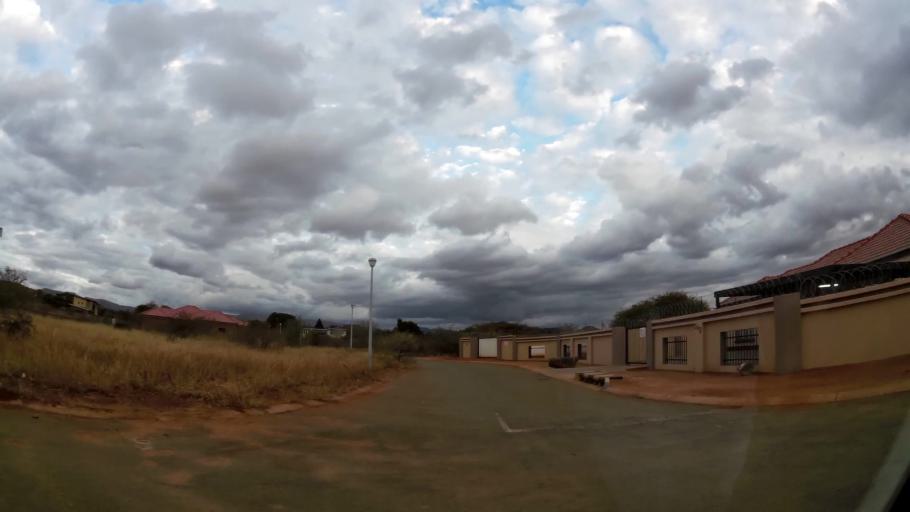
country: ZA
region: Limpopo
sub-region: Waterberg District Municipality
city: Mokopane
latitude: -24.1983
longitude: 29.0005
